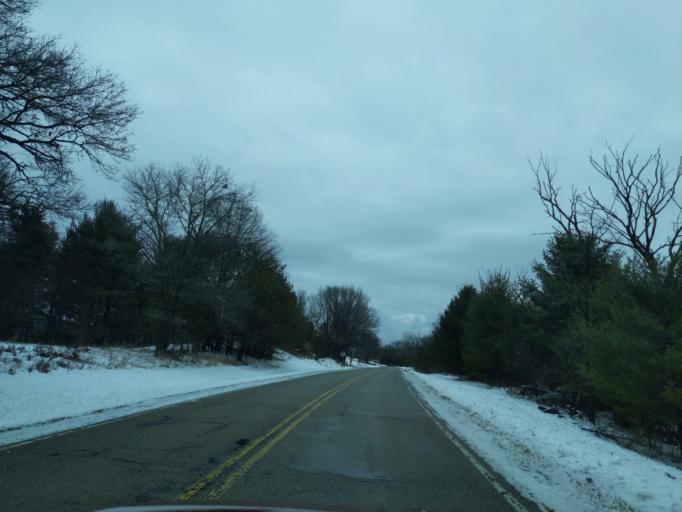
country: US
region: Wisconsin
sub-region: Marquette County
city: Montello
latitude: 43.9126
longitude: -89.3568
